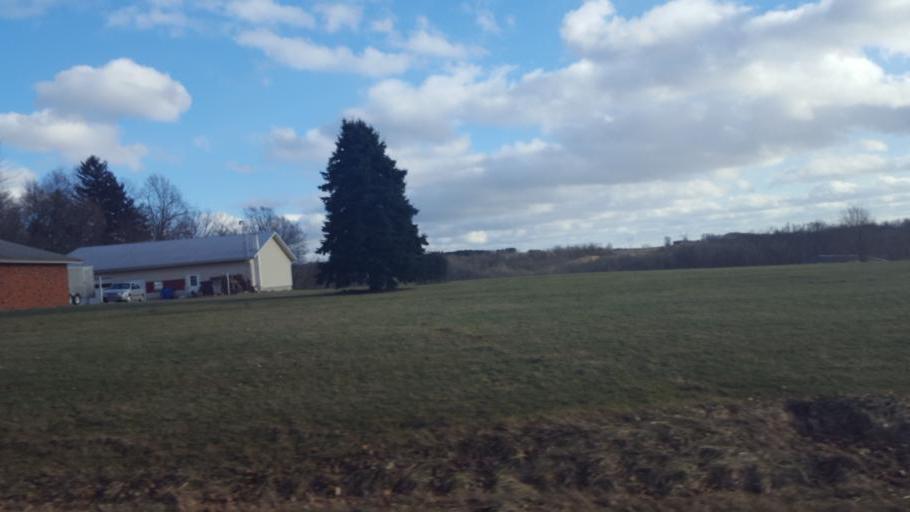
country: US
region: Ohio
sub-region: Knox County
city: Fredericktown
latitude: 40.4983
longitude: -82.5367
